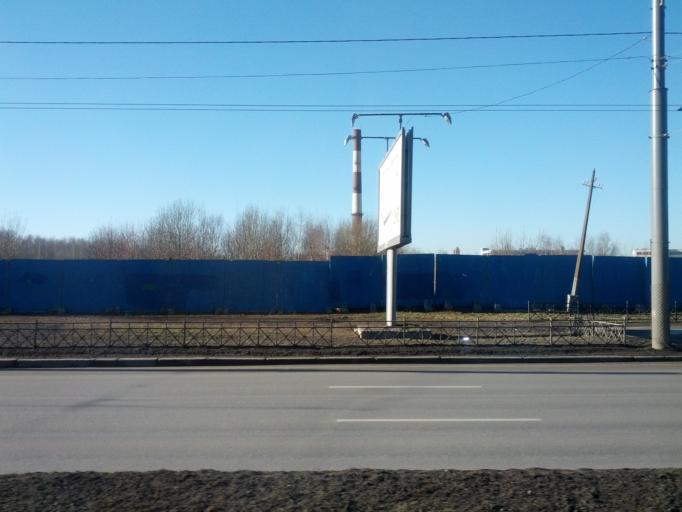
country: RU
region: St.-Petersburg
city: Centralniy
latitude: 59.9163
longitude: 30.4302
